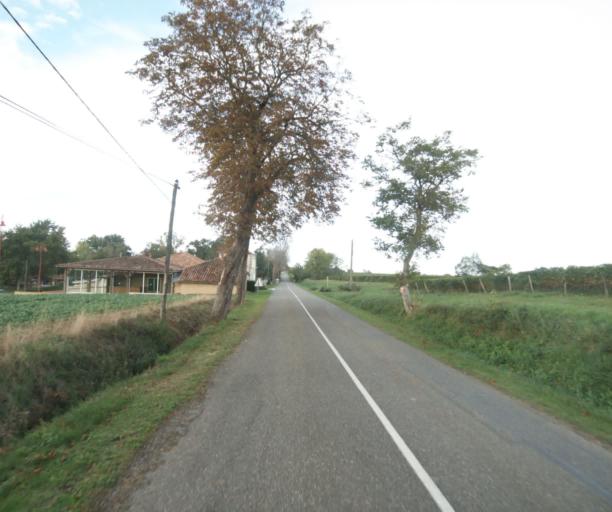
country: FR
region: Midi-Pyrenees
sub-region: Departement du Gers
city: Le Houga
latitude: 43.8459
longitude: -0.1356
